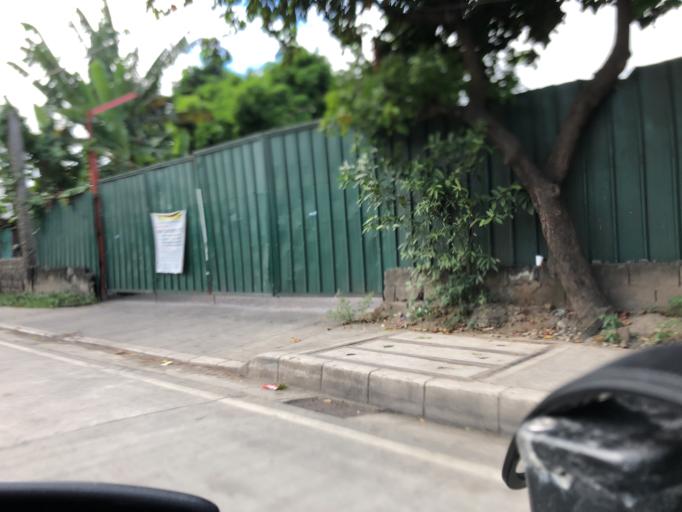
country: PH
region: Calabarzon
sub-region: Province of Rizal
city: San Mateo
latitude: 14.7389
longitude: 121.0604
